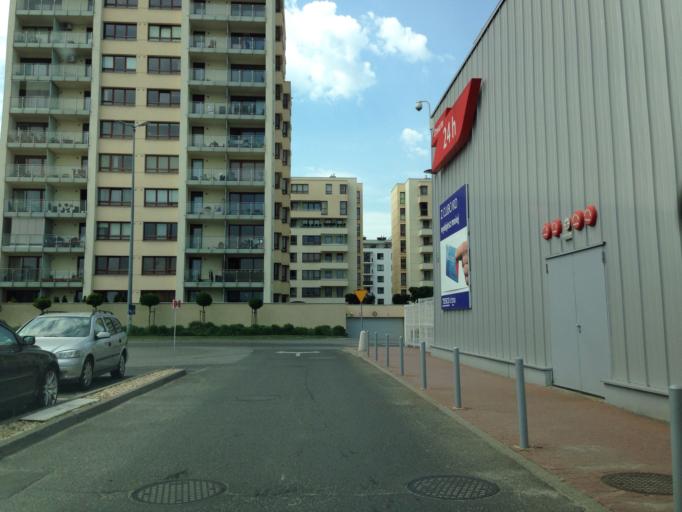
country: PL
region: Masovian Voivodeship
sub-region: Warszawa
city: Bemowo
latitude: 52.2397
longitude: 20.9041
